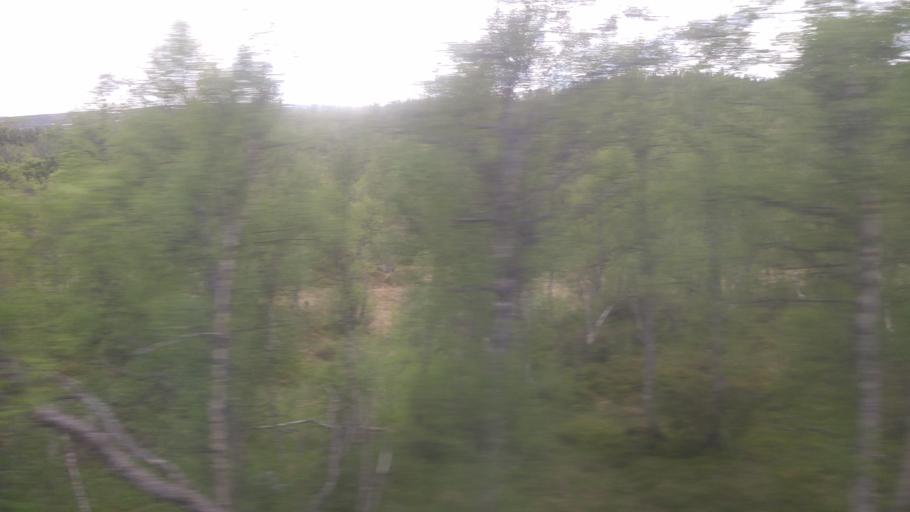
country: NO
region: Sor-Trondelag
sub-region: Holtalen
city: Alen
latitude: 62.7539
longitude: 11.3300
